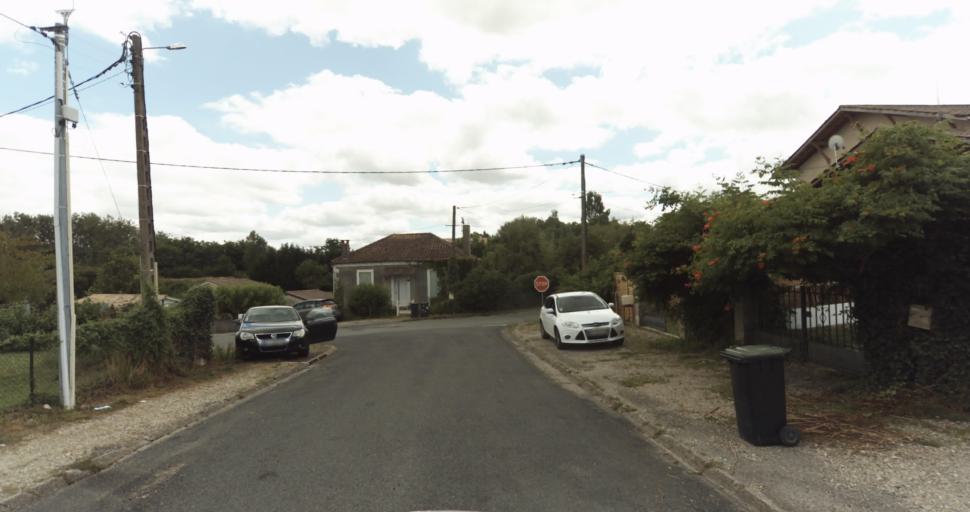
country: FR
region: Aquitaine
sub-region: Departement de la Gironde
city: Bazas
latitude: 44.4366
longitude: -0.2183
